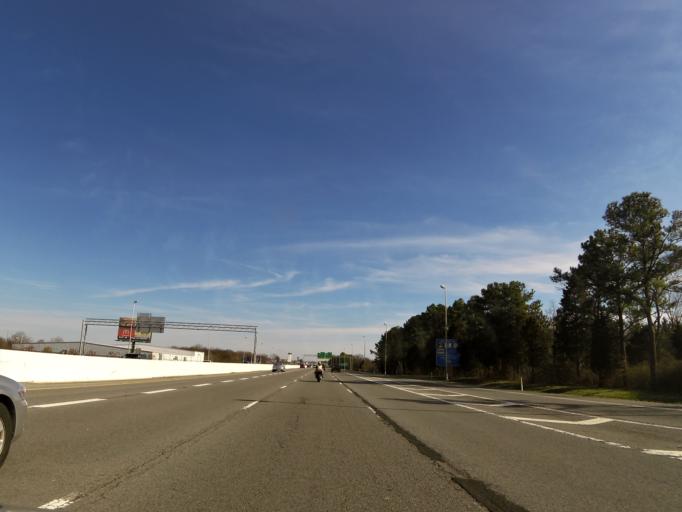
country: US
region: Tennessee
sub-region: Rutherford County
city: Murfreesboro
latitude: 35.8249
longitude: -86.4108
